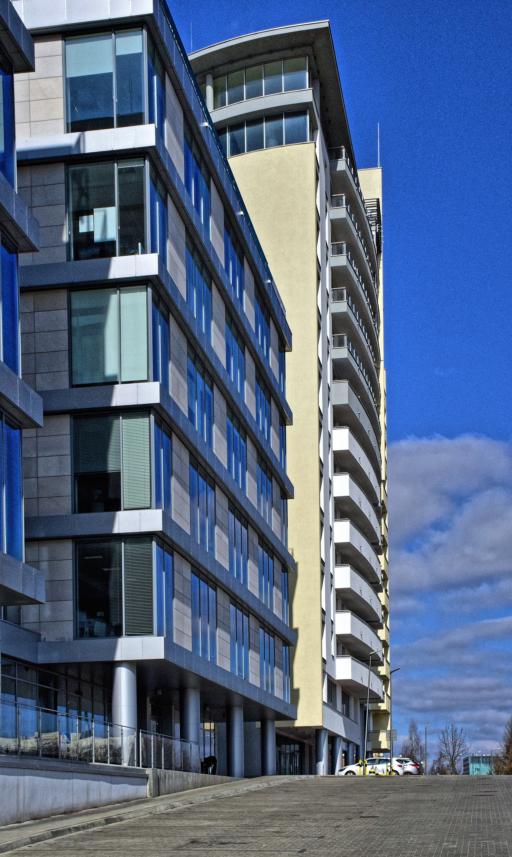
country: PL
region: Lublin Voivodeship
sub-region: Powiat lubelski
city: Lublin
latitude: 51.2558
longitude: 22.5581
